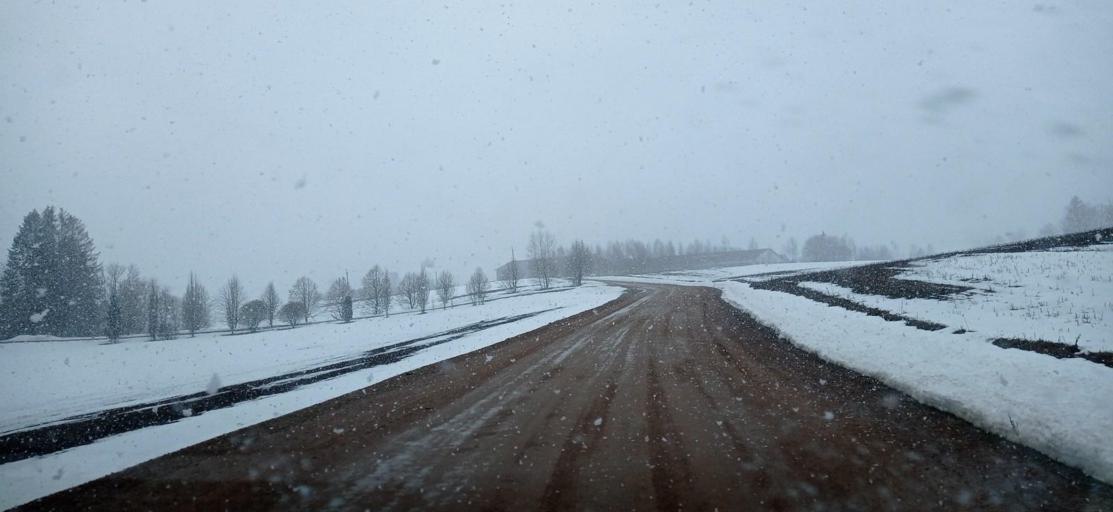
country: EE
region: Tartu
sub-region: Noo vald
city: Noo
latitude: 58.0924
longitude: 26.6668
